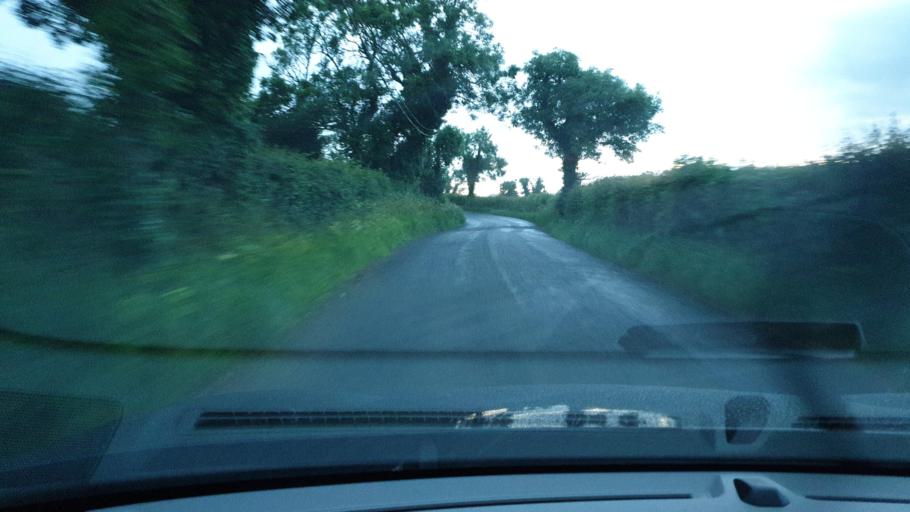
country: IE
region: Leinster
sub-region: An Mhi
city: Ashbourne
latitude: 53.5377
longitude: -6.3301
